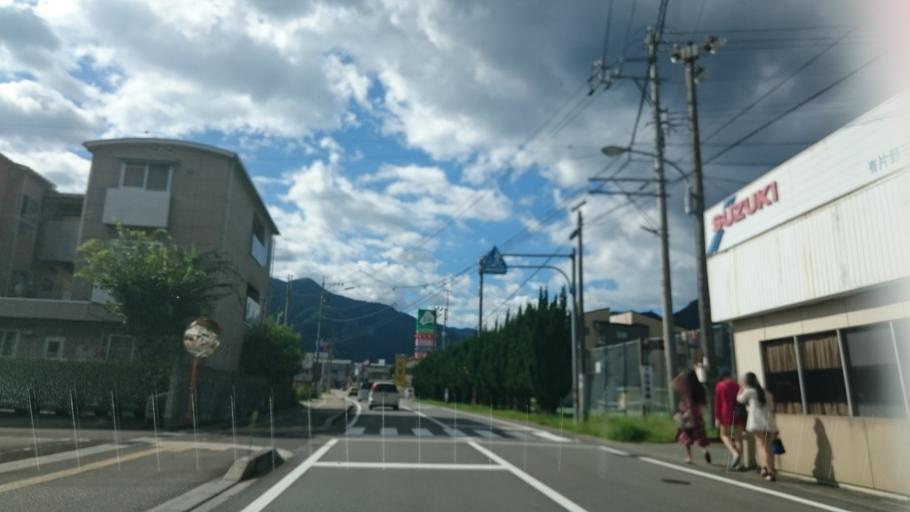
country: JP
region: Gifu
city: Gujo
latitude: 35.7996
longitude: 137.2510
